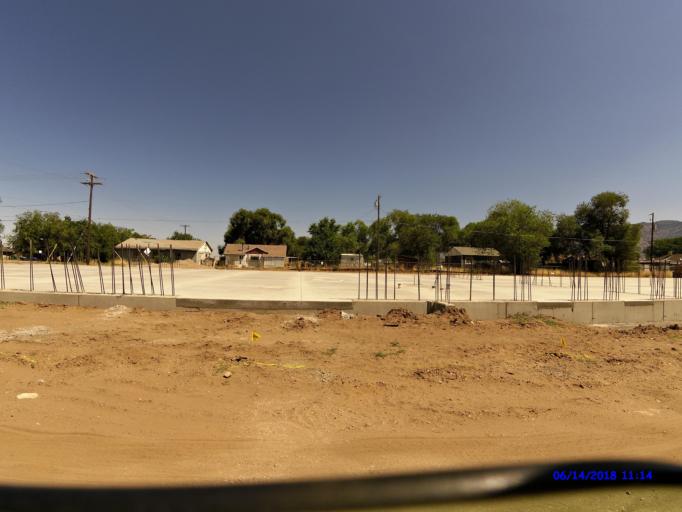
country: US
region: Utah
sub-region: Weber County
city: Ogden
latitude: 41.2169
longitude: -112.0004
